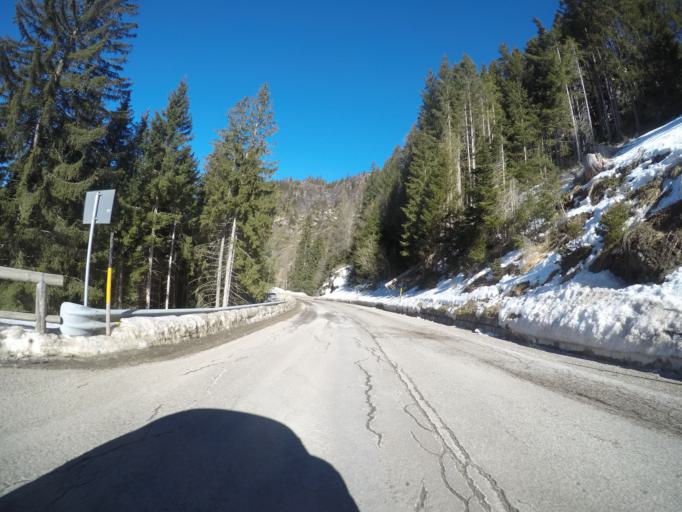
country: IT
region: Veneto
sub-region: Provincia di Belluno
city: Colle Santa Lucia
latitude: 46.4448
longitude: 12.0011
